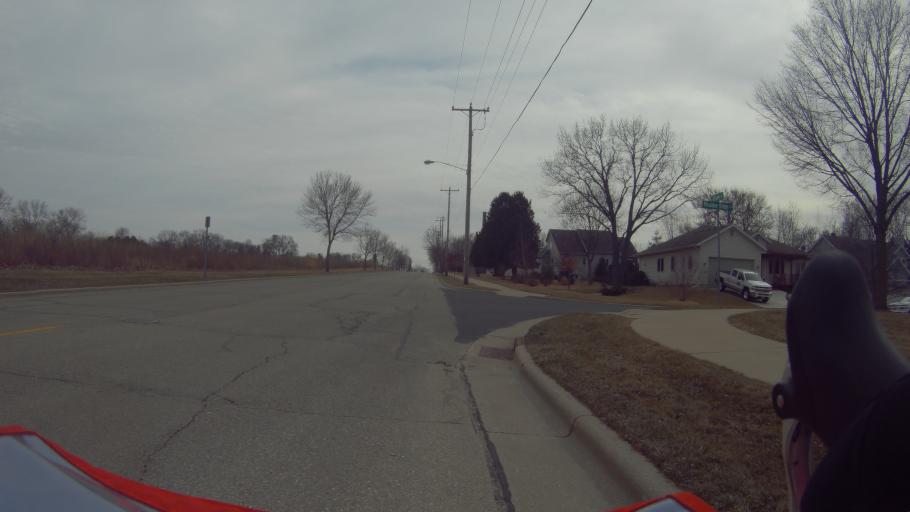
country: US
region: Wisconsin
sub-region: Dane County
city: Maple Bluff
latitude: 43.1379
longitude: -89.3978
